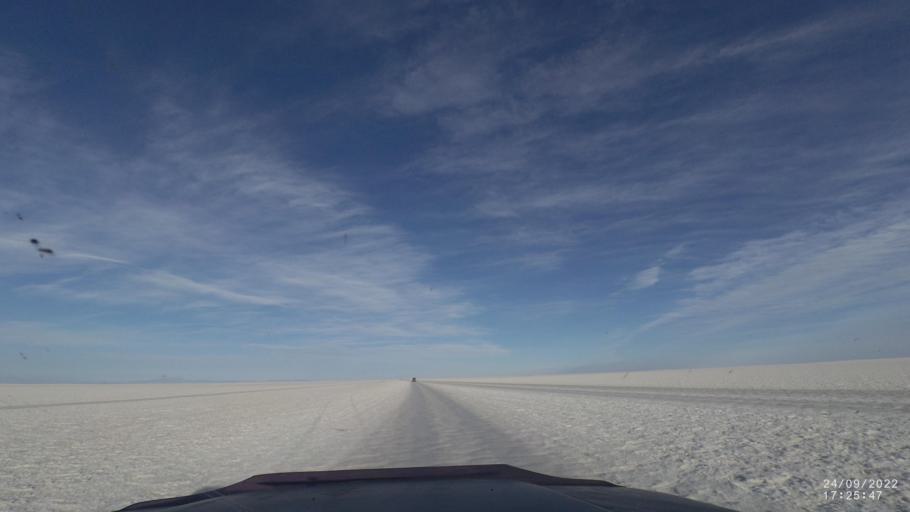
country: BO
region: Potosi
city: Colchani
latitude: -20.2905
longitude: -67.4807
